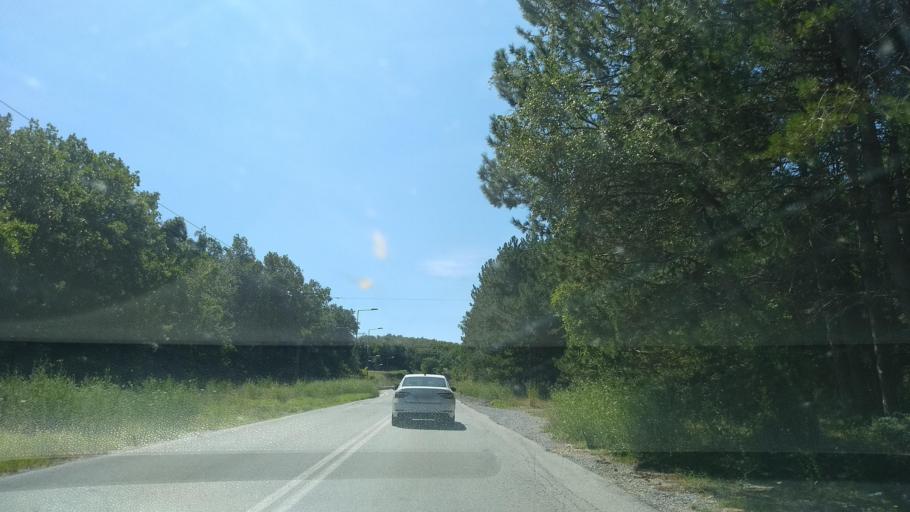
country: GR
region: Central Macedonia
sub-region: Nomos Chalkidikis
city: Megali Panagia
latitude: 40.4597
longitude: 23.6552
